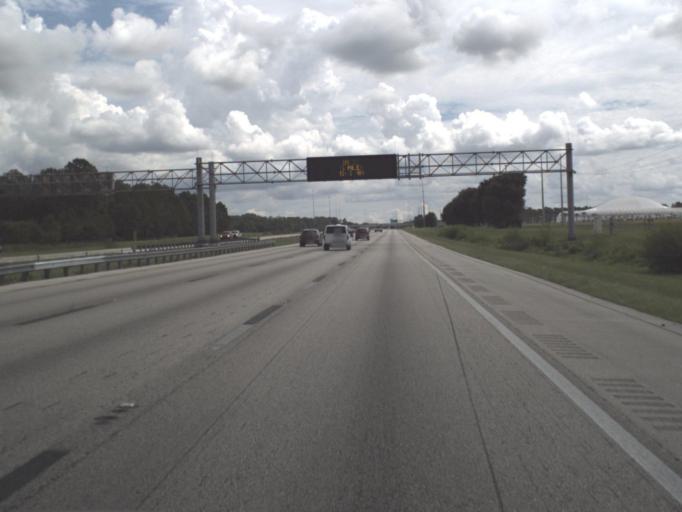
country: US
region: Florida
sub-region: Polk County
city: Polk City
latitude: 28.1501
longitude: -81.8617
